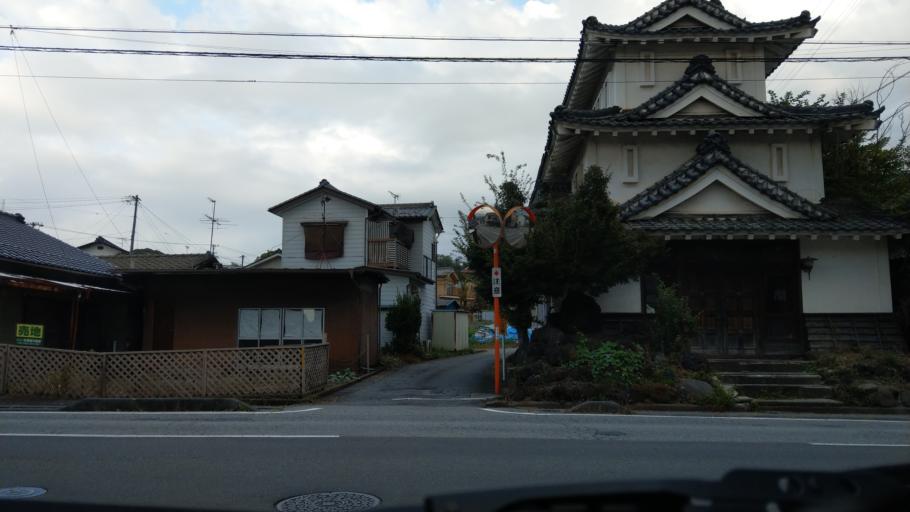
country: JP
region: Nagano
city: Komoro
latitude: 36.3210
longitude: 138.4329
